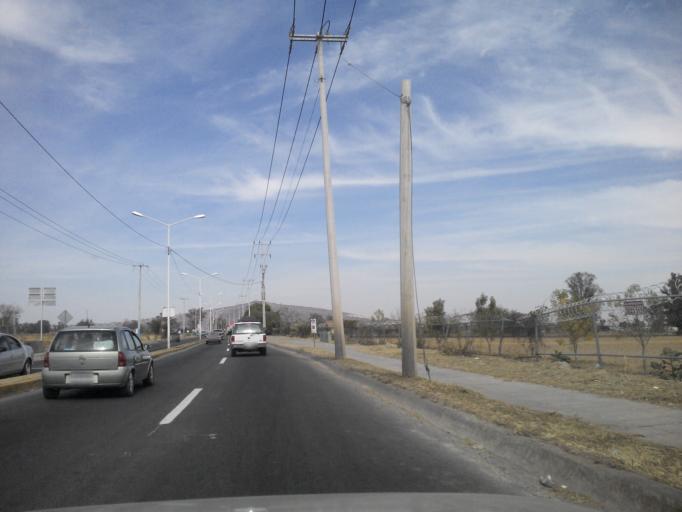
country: MX
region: Jalisco
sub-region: San Pedro Tlaquepaque
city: Paseo del Prado
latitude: 20.5543
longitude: -103.3970
